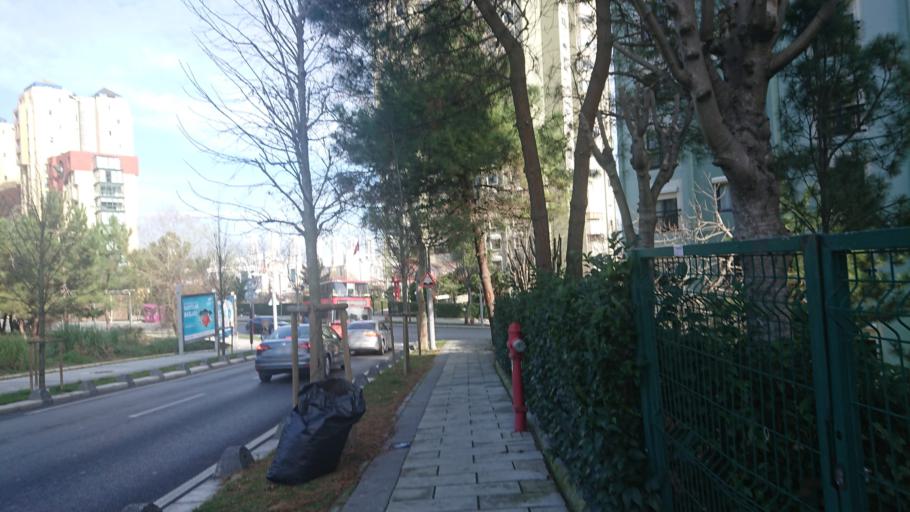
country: TR
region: Istanbul
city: Esenyurt
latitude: 41.0658
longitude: 28.6770
